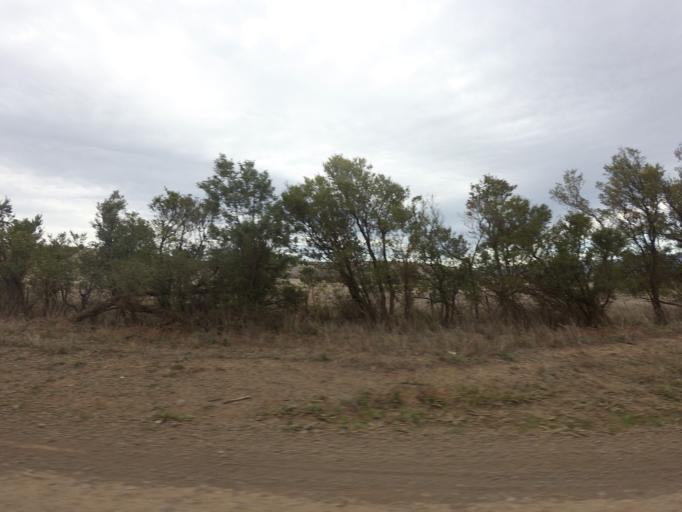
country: AU
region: Tasmania
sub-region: Derwent Valley
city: New Norfolk
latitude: -42.5537
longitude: 146.8932
